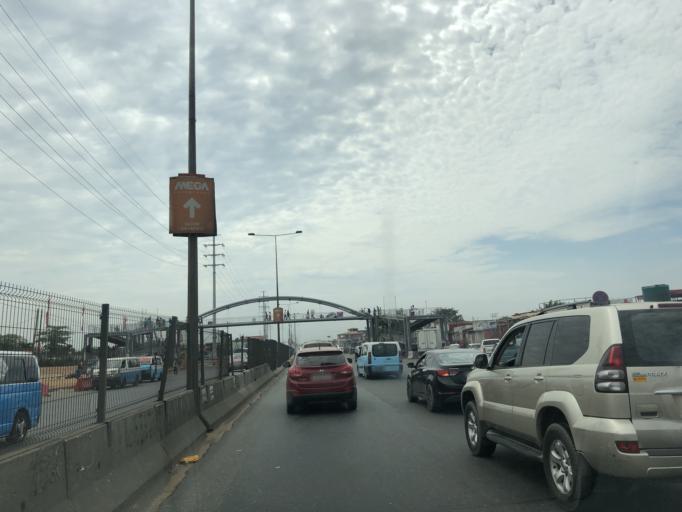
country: AO
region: Luanda
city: Luanda
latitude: -8.8479
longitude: 13.2829
